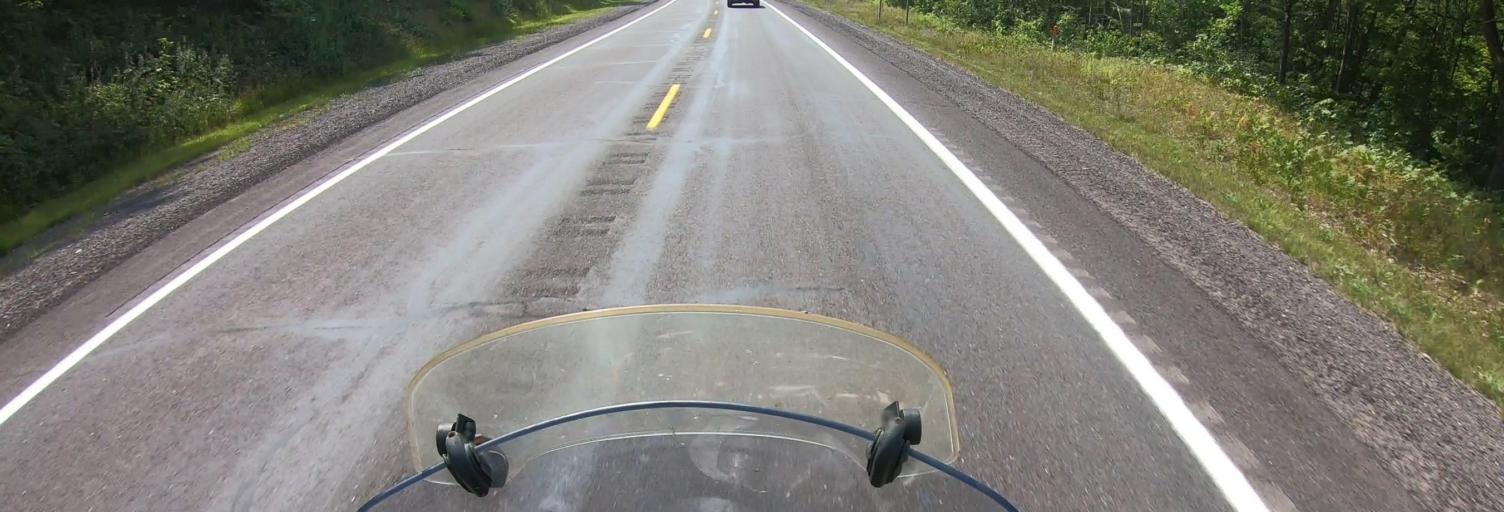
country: US
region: Michigan
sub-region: Houghton County
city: Hancock
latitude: 46.8698
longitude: -88.8924
